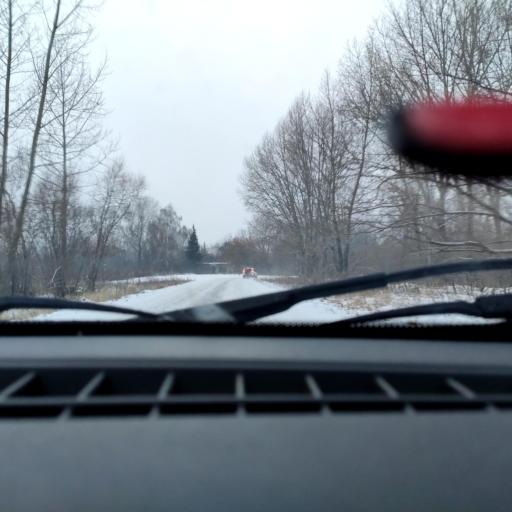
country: RU
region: Bashkortostan
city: Blagoveshchensk
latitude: 54.9054
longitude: 56.0112
